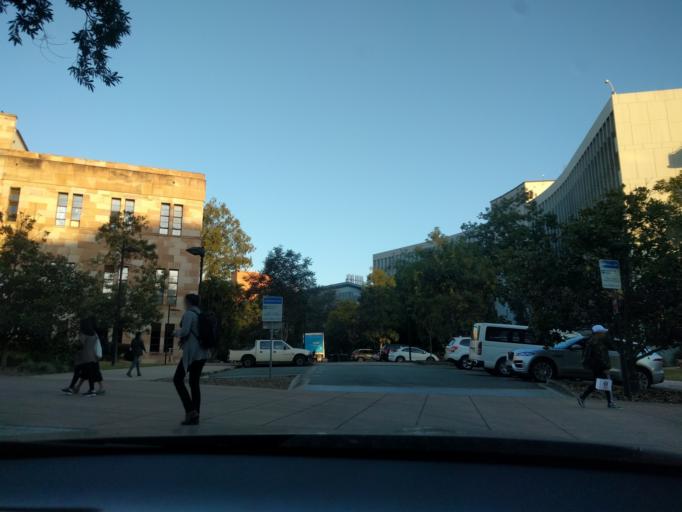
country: AU
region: Queensland
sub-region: Brisbane
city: Yeronga
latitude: -27.4977
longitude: 153.0114
